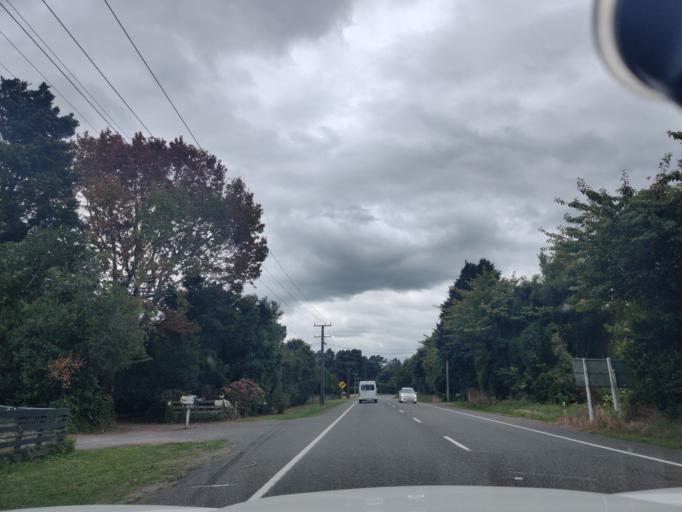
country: NZ
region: Manawatu-Wanganui
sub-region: Horowhenua District
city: Levin
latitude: -40.6539
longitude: 175.2835
